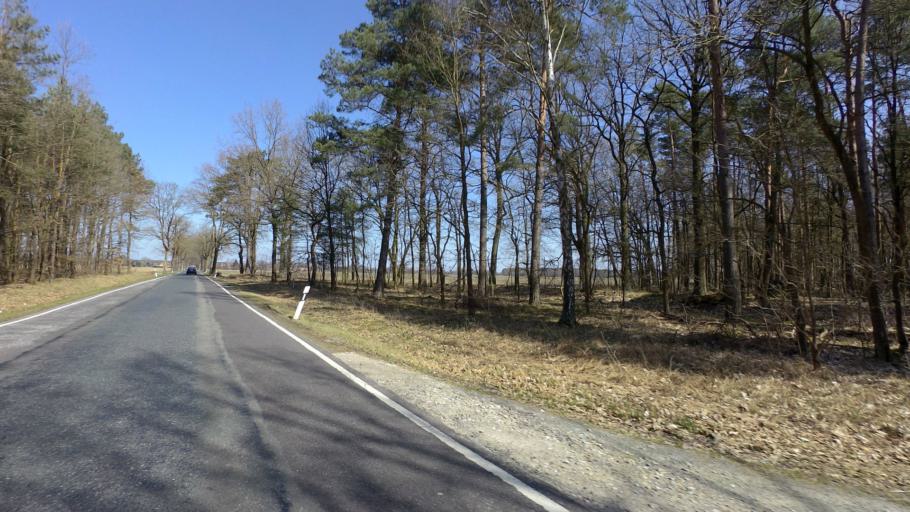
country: DE
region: Brandenburg
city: Lindow
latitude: 52.9233
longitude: 12.9633
